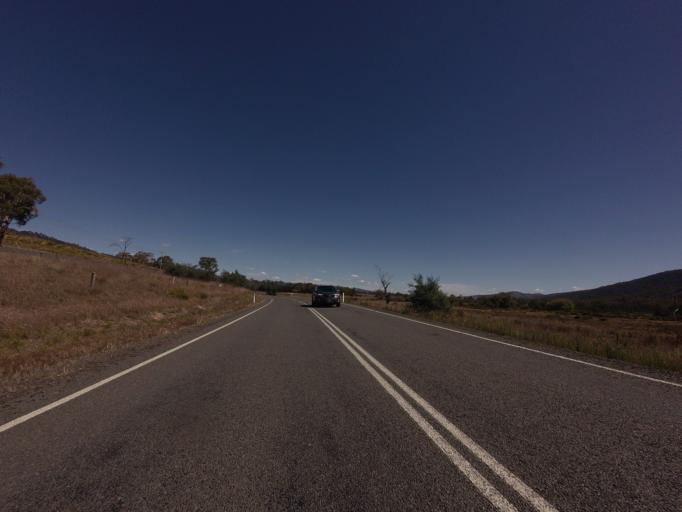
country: AU
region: Tasmania
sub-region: Northern Midlands
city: Evandale
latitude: -41.7470
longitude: 147.7827
